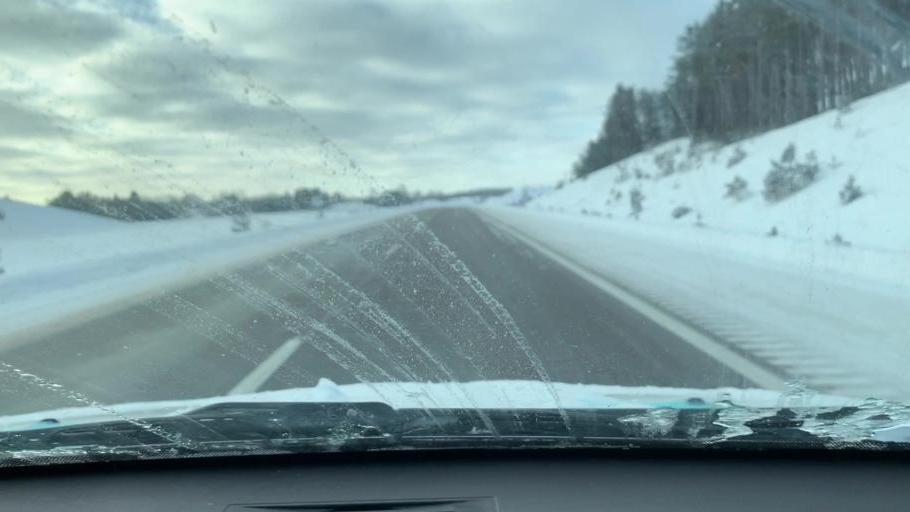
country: US
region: Michigan
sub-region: Wexford County
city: Manton
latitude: 44.3918
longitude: -85.3828
